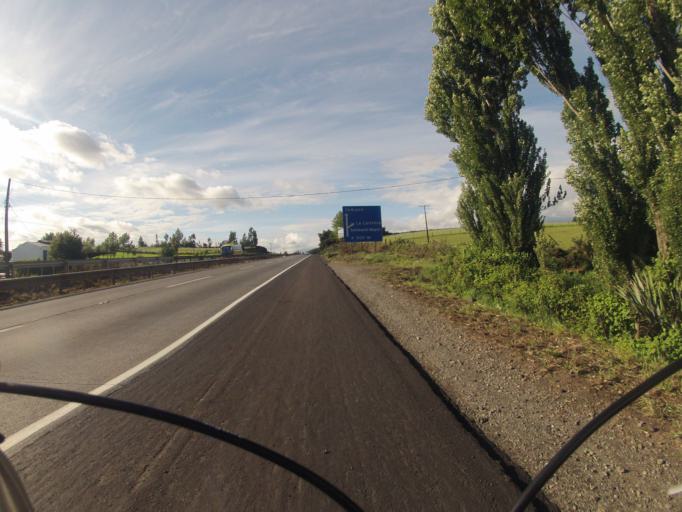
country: CL
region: Araucania
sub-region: Provincia de Cautin
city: Temuco
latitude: -38.8151
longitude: -72.6245
